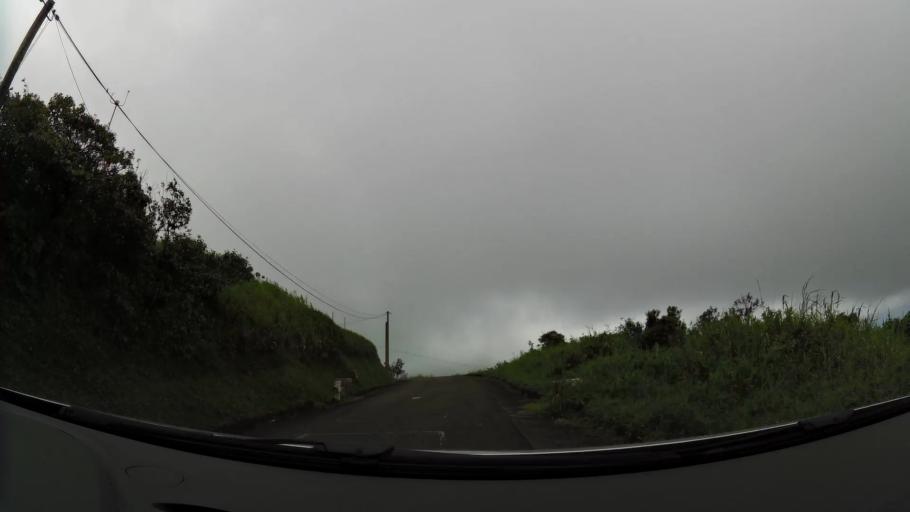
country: MQ
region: Martinique
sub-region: Martinique
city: Le Morne-Rouge
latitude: 14.8058
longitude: -61.1511
